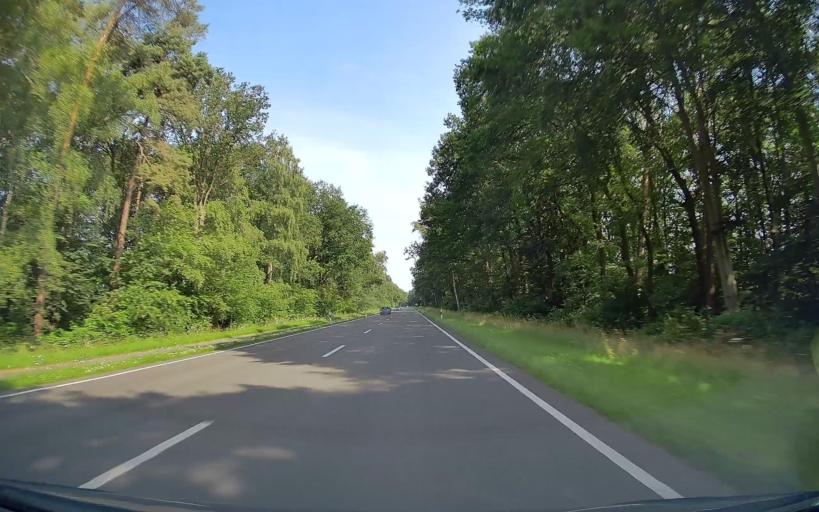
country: DE
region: Lower Saxony
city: Molbergen
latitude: 52.9297
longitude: 7.9490
